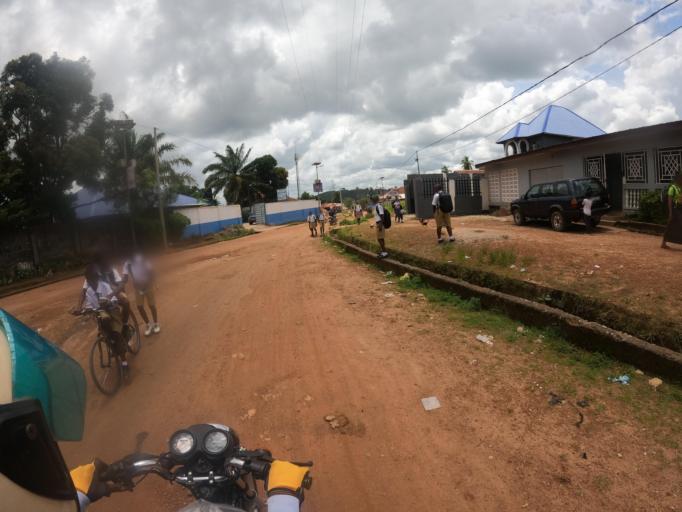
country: SL
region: Northern Province
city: Makeni
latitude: 8.8928
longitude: -12.0491
